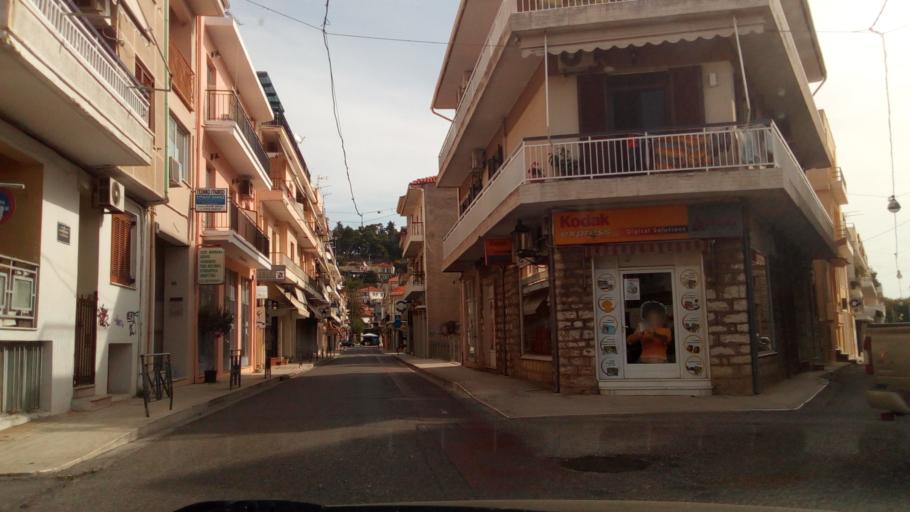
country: GR
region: West Greece
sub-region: Nomos Aitolias kai Akarnanias
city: Nafpaktos
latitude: 38.3937
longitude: 21.8319
